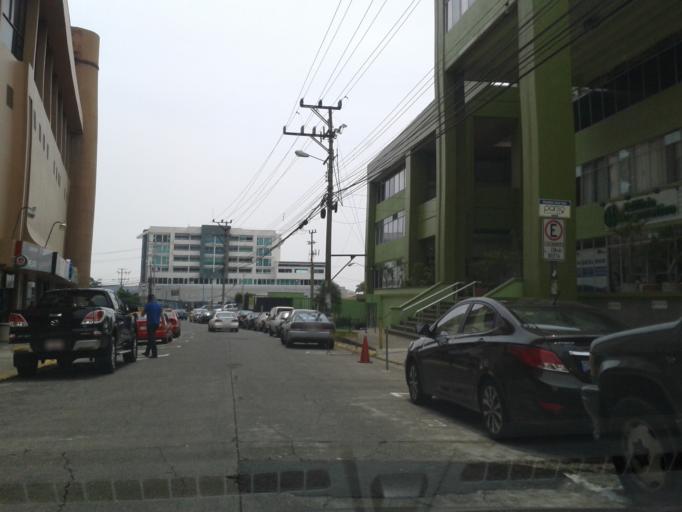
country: CR
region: San Jose
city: San Pedro
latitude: 9.9347
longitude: -84.0560
